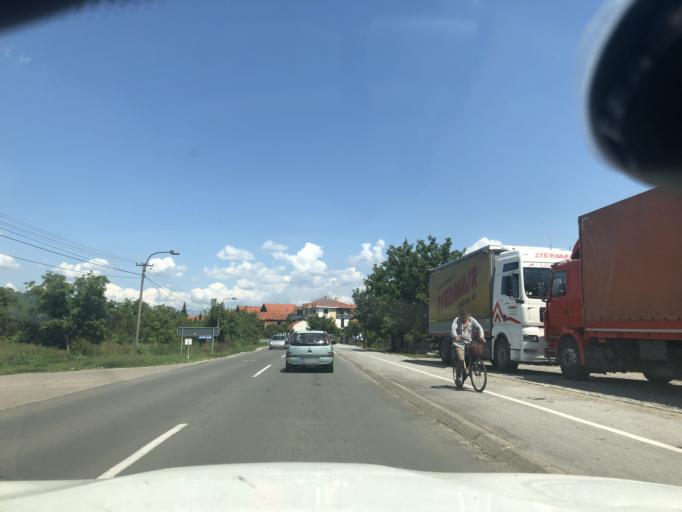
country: RS
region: Central Serbia
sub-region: Jablanicki Okrug
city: Leskovac
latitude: 42.9866
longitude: 21.9216
